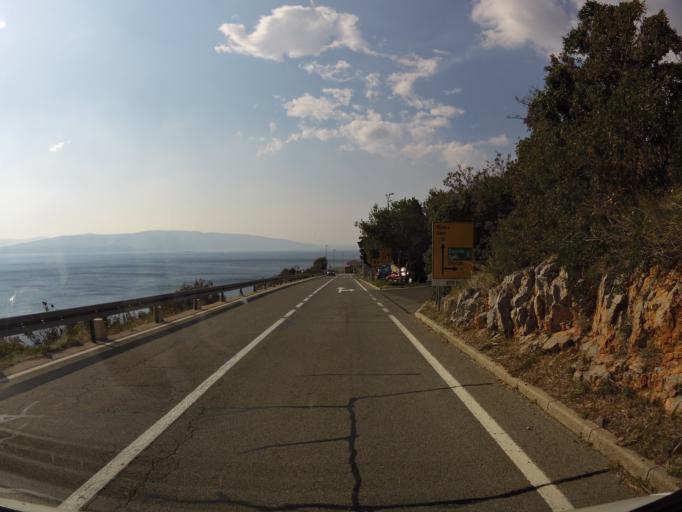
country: HR
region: Licko-Senjska
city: Senj
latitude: 44.9822
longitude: 14.9086
